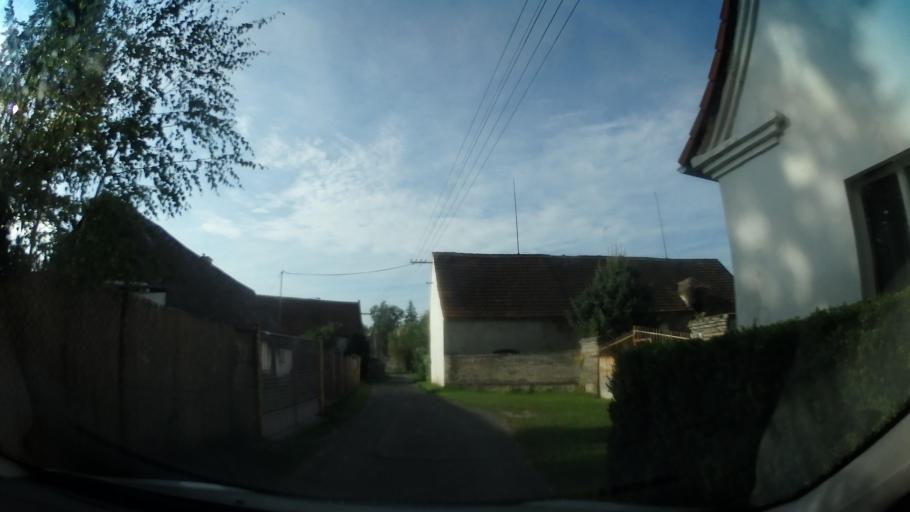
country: CZ
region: Jihocesky
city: Cimelice
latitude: 49.4251
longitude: 14.1213
